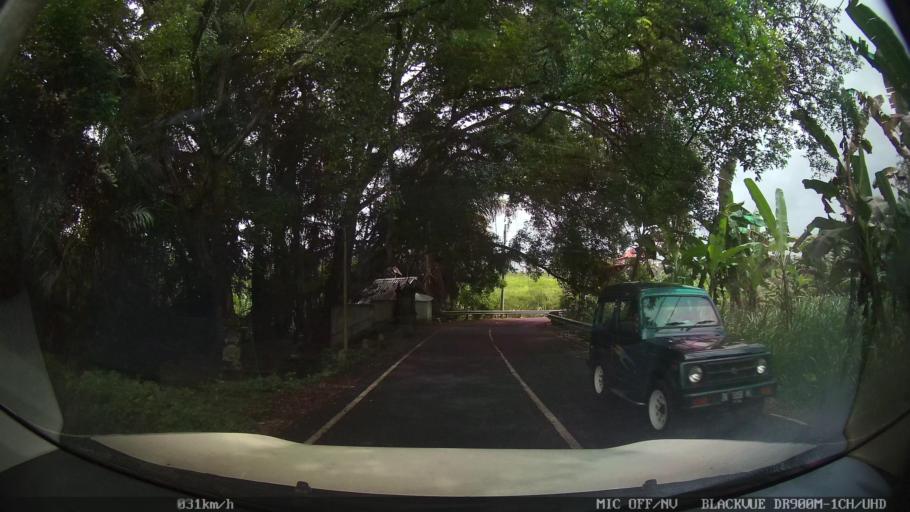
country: ID
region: Bali
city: Banjar Serangan
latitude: -8.5331
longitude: 115.1740
